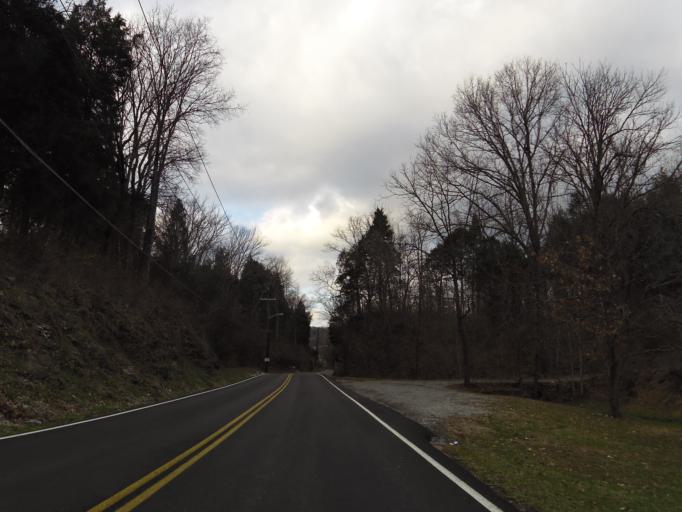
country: US
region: Tennessee
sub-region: Knox County
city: Knoxville
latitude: 35.9298
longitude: -83.8688
